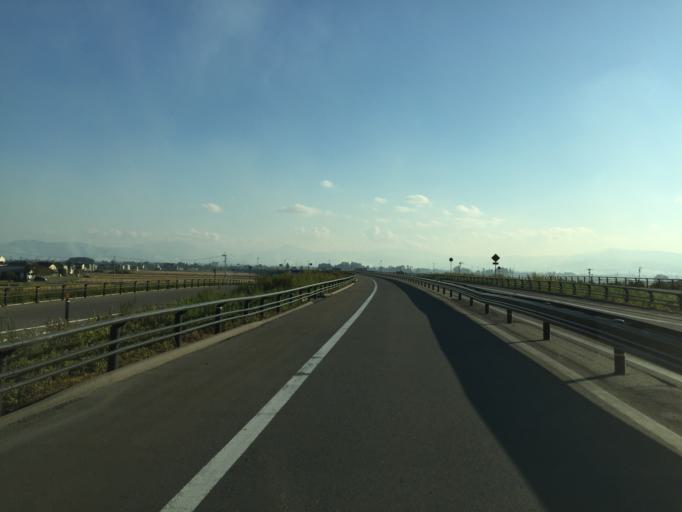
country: JP
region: Fukushima
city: Kitakata
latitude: 37.6029
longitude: 139.8762
